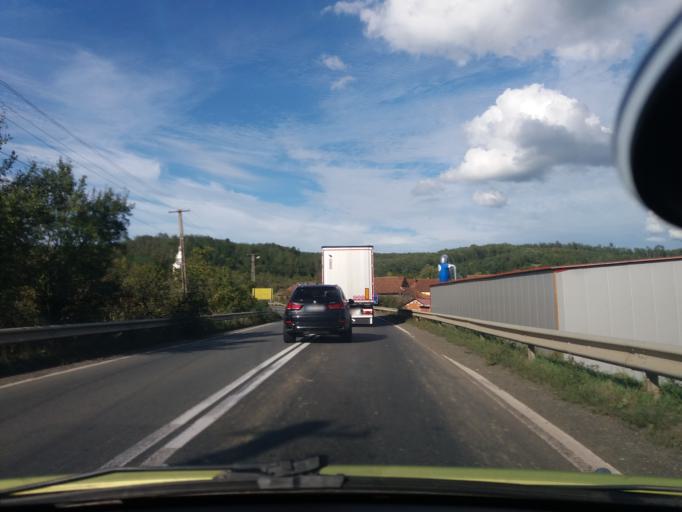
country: RO
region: Arad
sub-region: Comuna Barzava
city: Barzava
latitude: 46.0869
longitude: 22.0247
